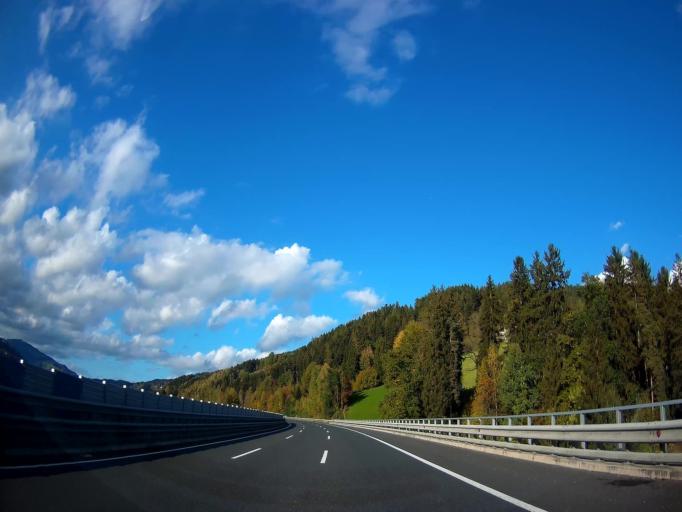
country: AT
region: Carinthia
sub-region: Politischer Bezirk Wolfsberg
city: Wolfsberg
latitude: 46.8650
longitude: 14.8358
